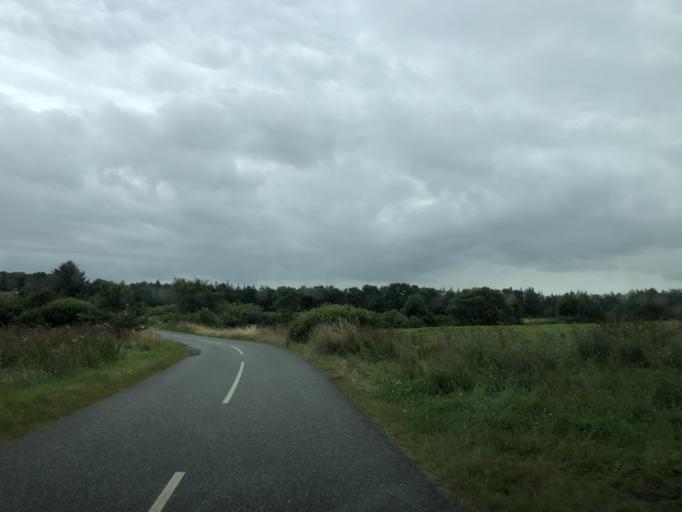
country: DK
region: Central Jutland
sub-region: Herning Kommune
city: Vildbjerg
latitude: 56.2020
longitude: 8.8430
